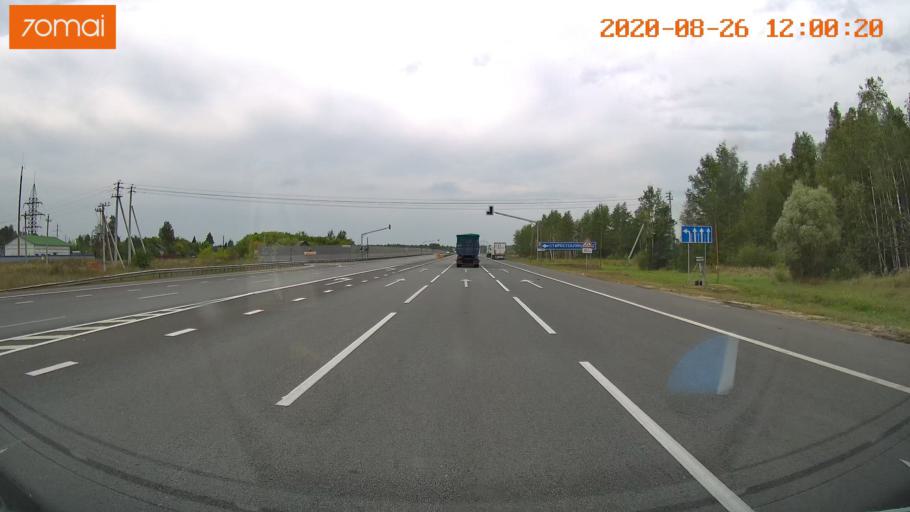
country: RU
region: Rjazan
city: Kiritsy
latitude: 54.2872
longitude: 40.2764
